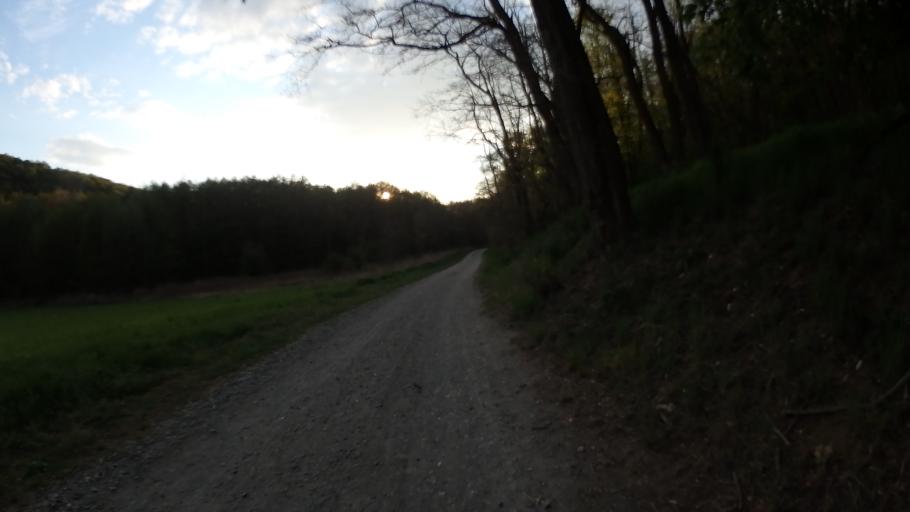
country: CZ
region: South Moravian
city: Strelice
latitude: 49.1421
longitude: 16.4851
